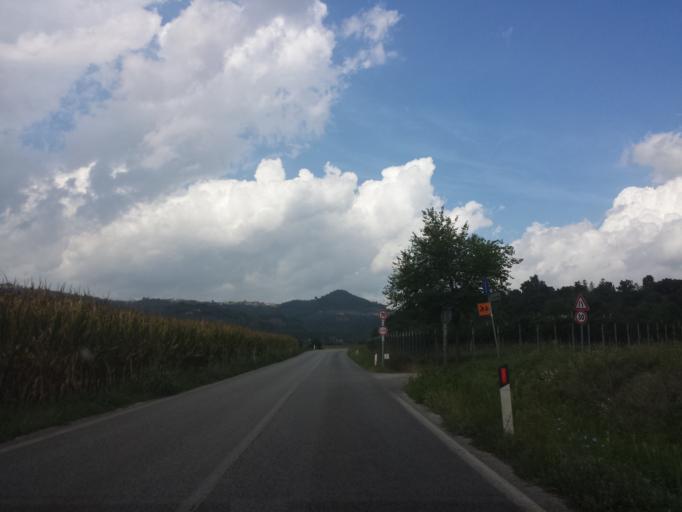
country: IT
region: Veneto
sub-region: Provincia di Vicenza
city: Sovizzo
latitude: 45.5479
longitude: 11.4291
